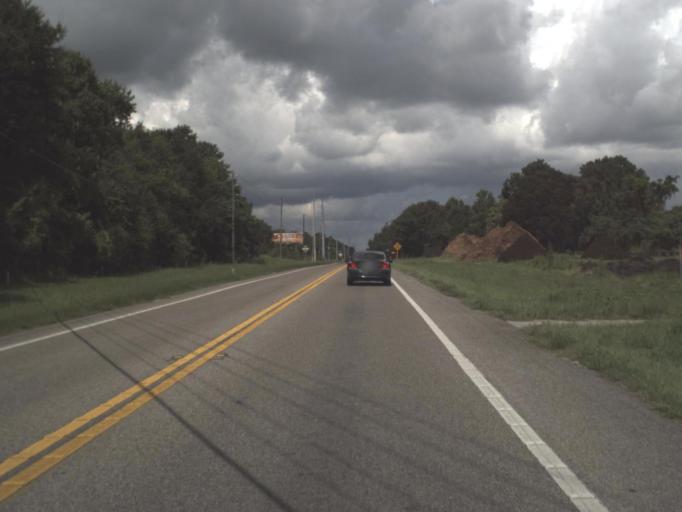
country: US
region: Florida
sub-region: Pasco County
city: San Antonio
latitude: 28.3246
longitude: -82.3334
